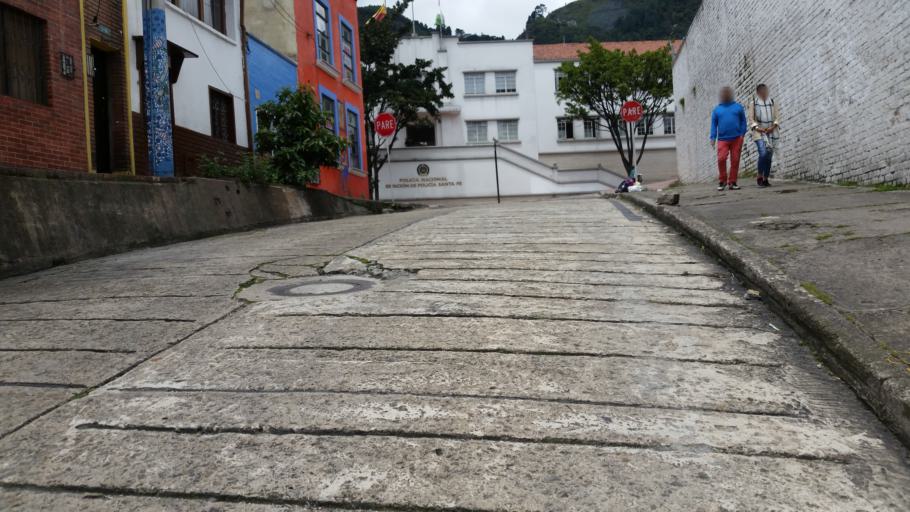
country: CO
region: Bogota D.C.
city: Bogota
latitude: 4.6155
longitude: -74.0669
